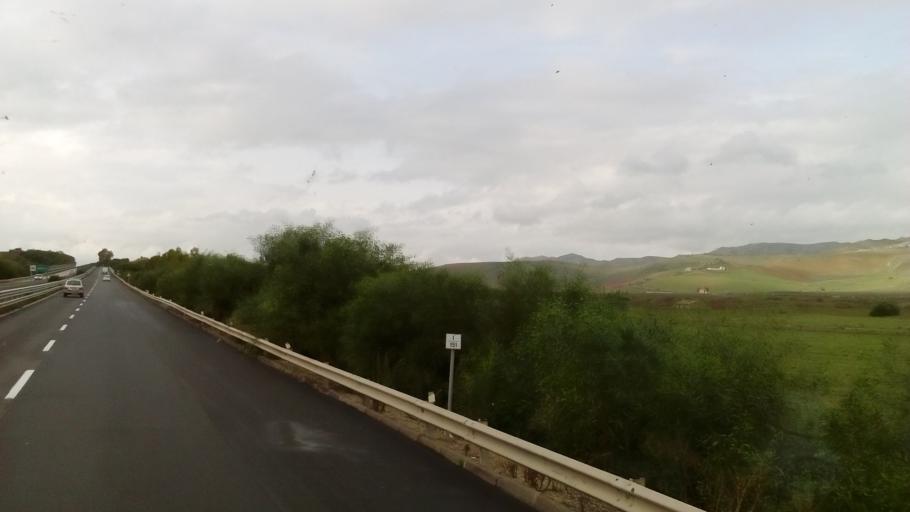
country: IT
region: Sicily
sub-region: Enna
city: Catenanuova
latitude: 37.5644
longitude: 14.6267
